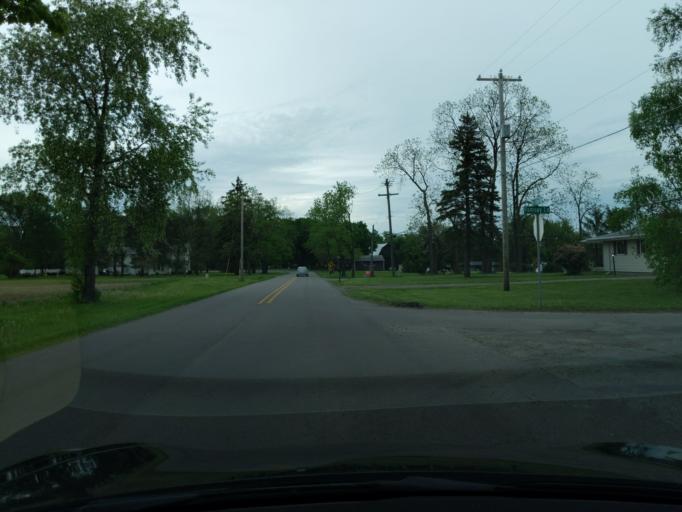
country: US
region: Michigan
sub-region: Ingham County
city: Leslie
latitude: 42.3858
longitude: -84.3493
